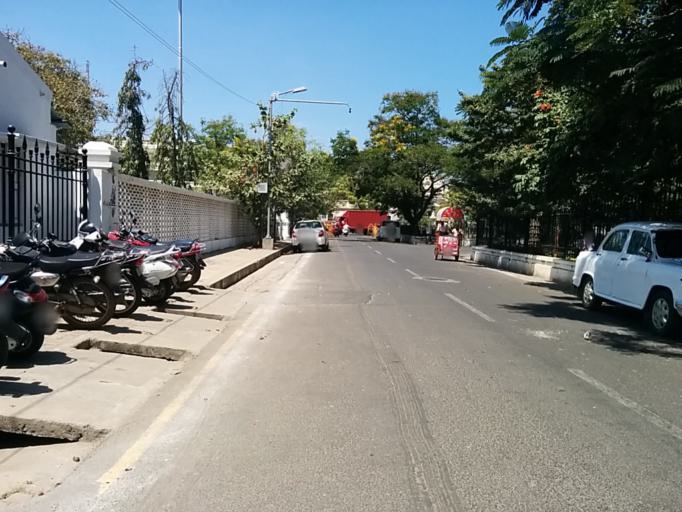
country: IN
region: Pondicherry
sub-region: Puducherry
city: Puducherry
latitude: 11.9336
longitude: 79.8334
